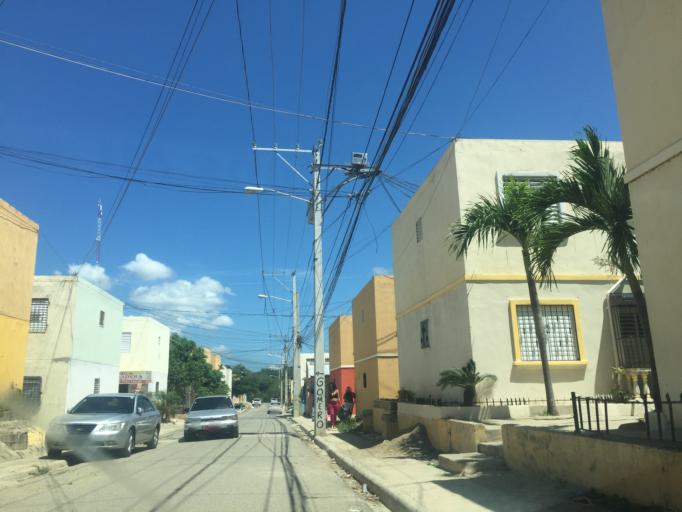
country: DO
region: Santiago
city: Santiago de los Caballeros
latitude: 19.4418
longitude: -70.7422
